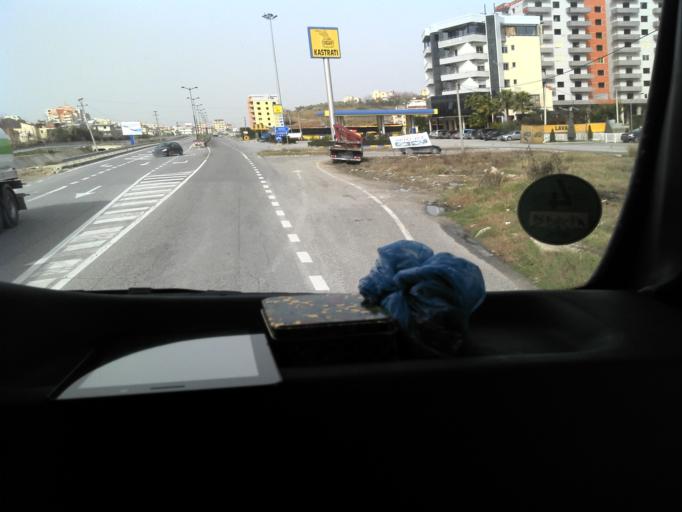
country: AL
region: Durres
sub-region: Rrethi i Durresit
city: Rrashbull
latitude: 41.2953
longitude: 19.5083
